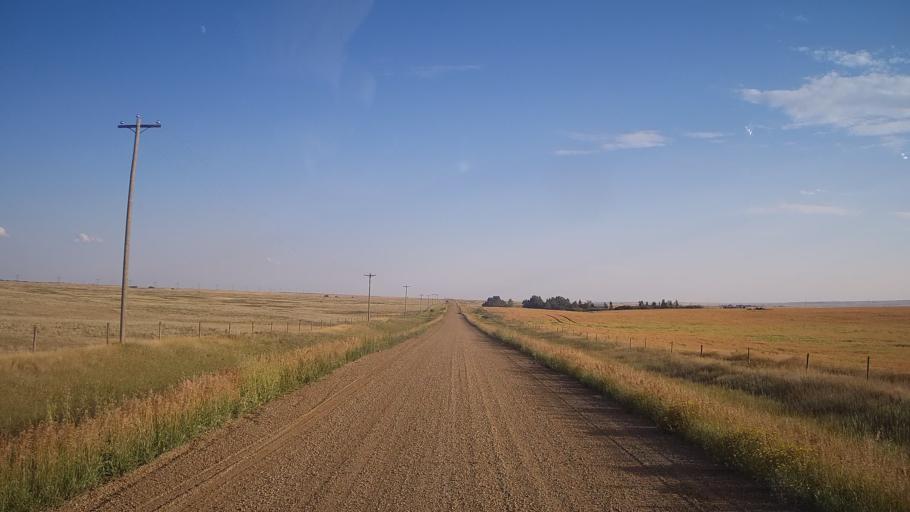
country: CA
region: Alberta
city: Hanna
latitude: 51.6193
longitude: -111.8569
